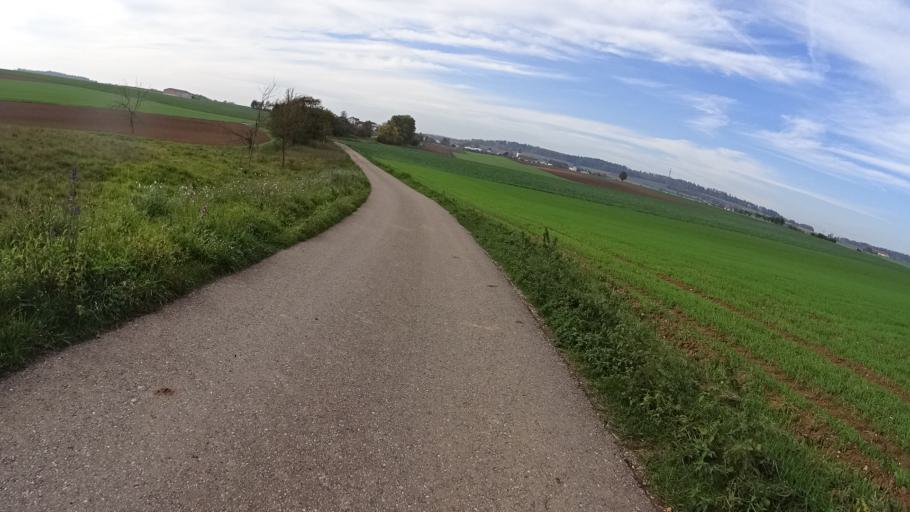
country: DE
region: Bavaria
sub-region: Upper Bavaria
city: Adelschlag
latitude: 48.8561
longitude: 11.2533
